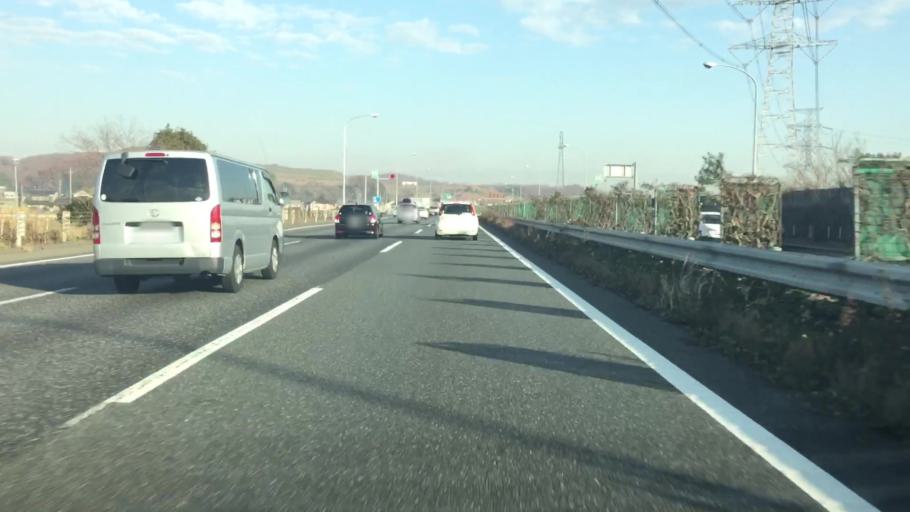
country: JP
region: Saitama
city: Sakado
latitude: 35.9739
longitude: 139.3800
